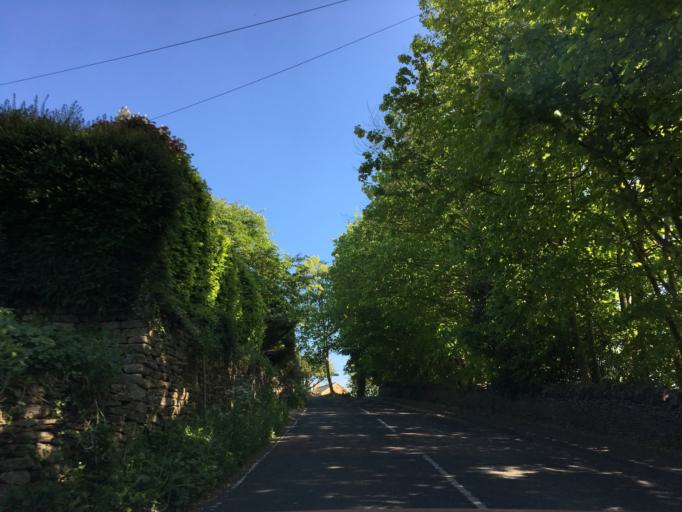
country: GB
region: England
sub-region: Gloucestershire
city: Nailsworth
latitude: 51.7133
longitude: -2.2276
